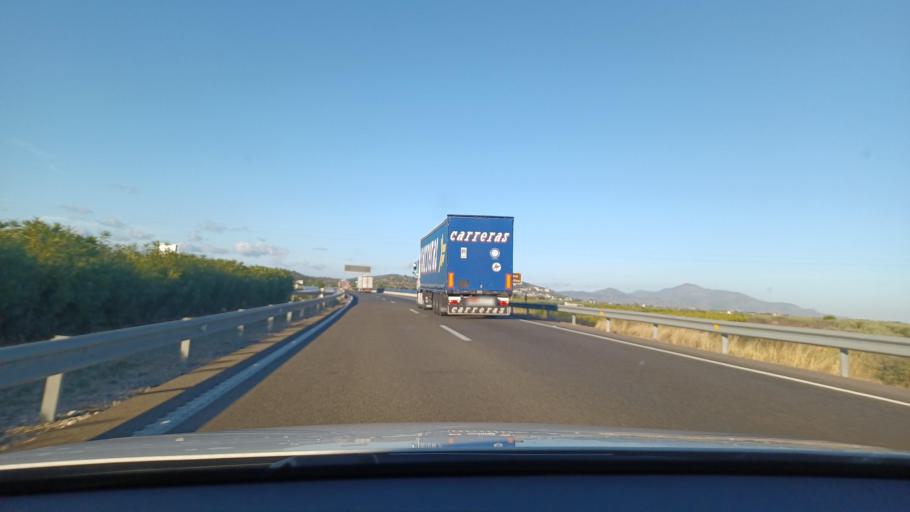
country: ES
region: Valencia
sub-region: Provincia de Castello
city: Vinaros
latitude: 40.4749
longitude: 0.4189
